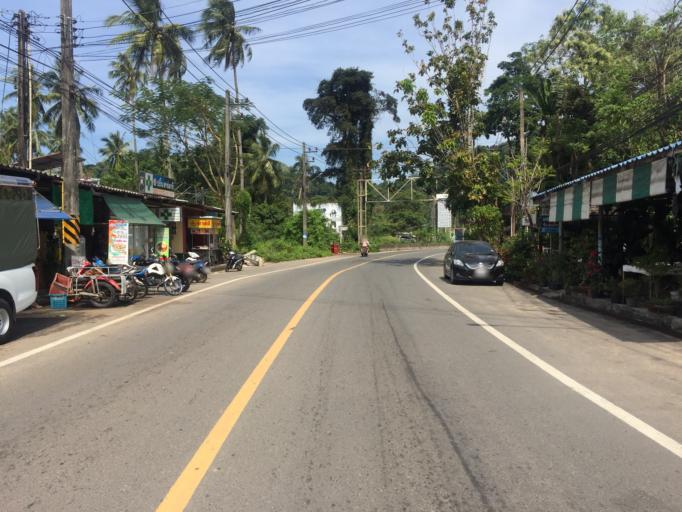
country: TH
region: Trat
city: Laem Ngop
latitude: 12.1321
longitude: 102.2753
